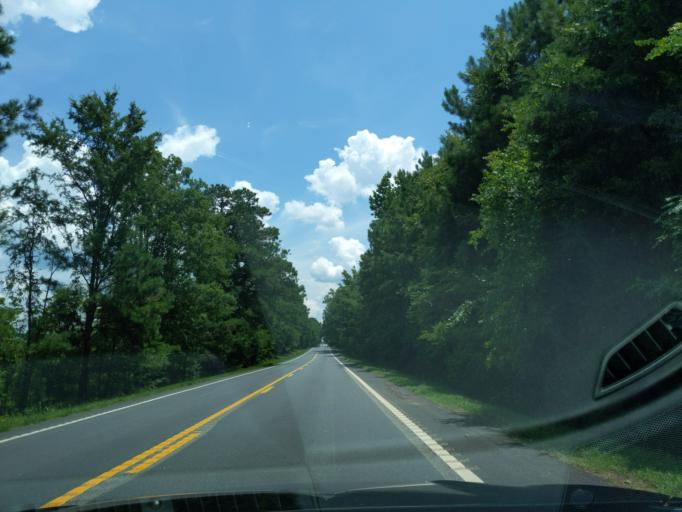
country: US
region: South Carolina
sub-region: Edgefield County
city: Edgefield
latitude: 33.8517
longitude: -81.9812
